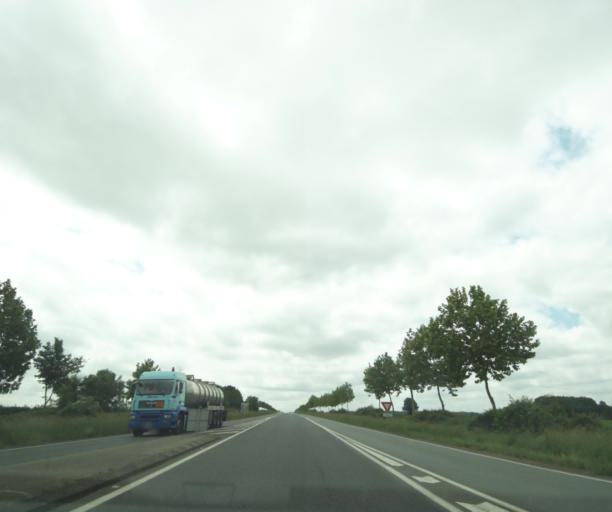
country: FR
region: Poitou-Charentes
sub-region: Departement des Deux-Sevres
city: Saint-Varent
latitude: 46.8471
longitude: -0.2089
